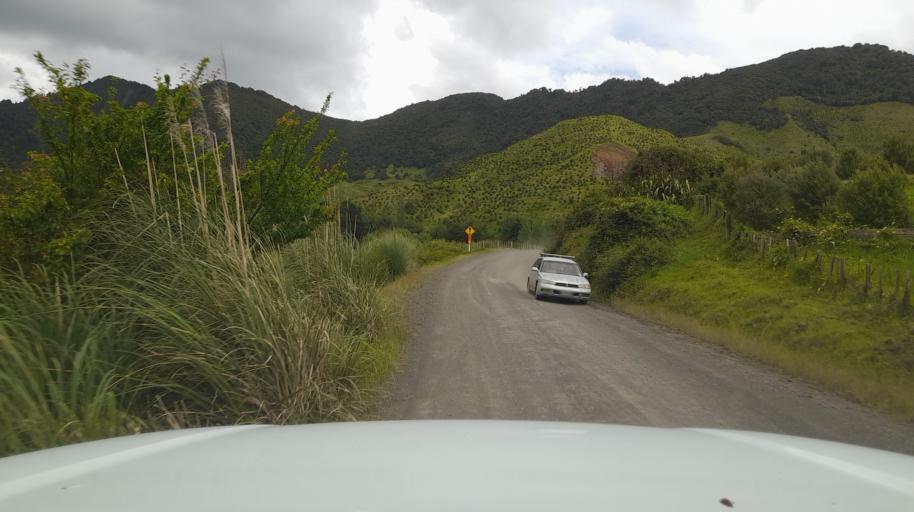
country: NZ
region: Northland
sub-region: Far North District
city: Kaitaia
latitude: -35.3311
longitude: 173.3548
